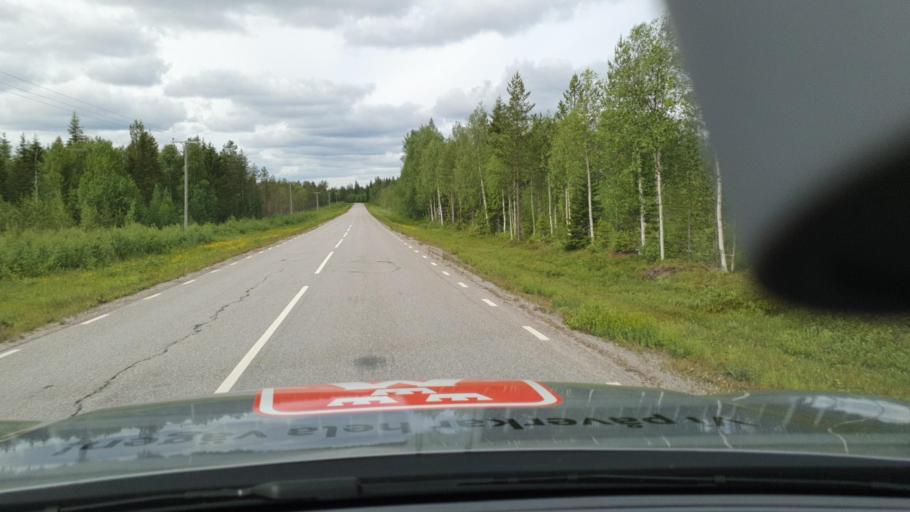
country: FI
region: Lapland
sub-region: Torniolaakso
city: Ylitornio
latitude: 66.0423
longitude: 23.5855
